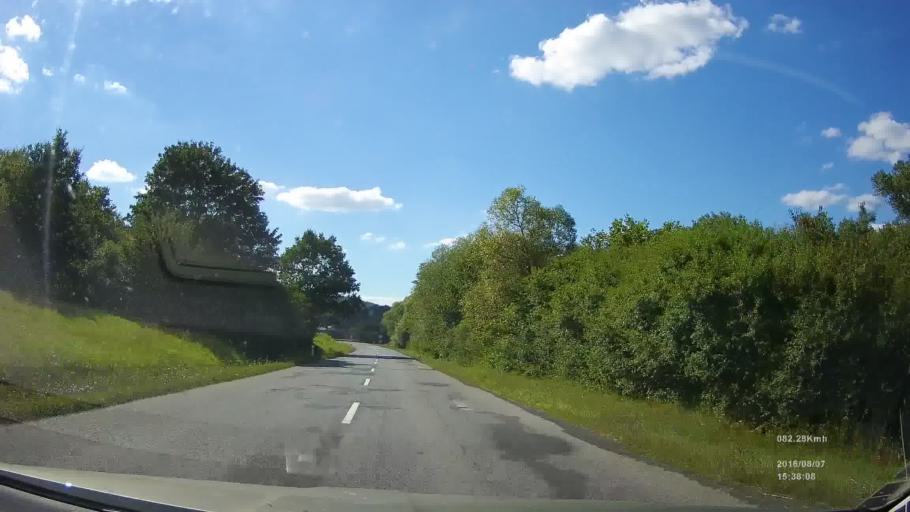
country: SK
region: Presovsky
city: Stropkov
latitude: 49.1125
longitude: 21.6166
